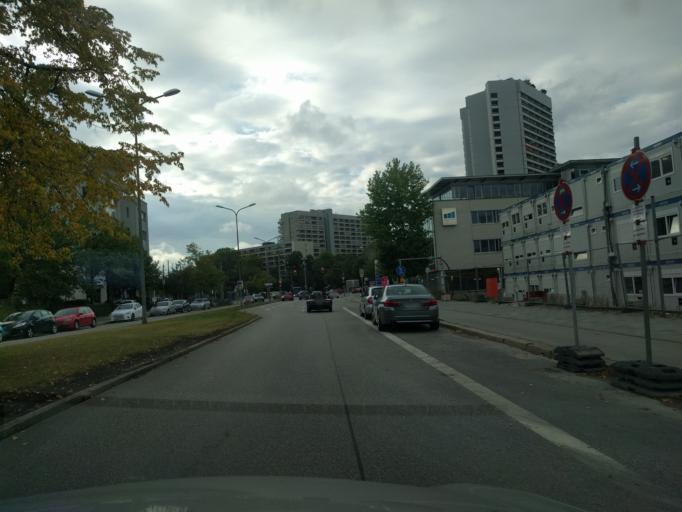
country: DE
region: Bavaria
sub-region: Upper Bavaria
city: Munich
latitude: 48.1335
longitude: 11.5240
